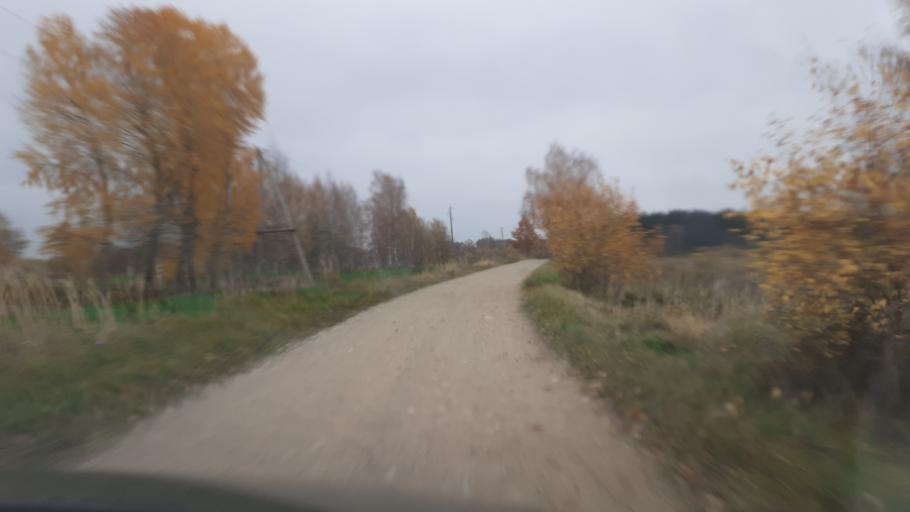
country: LV
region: Saldus Rajons
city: Saldus
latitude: 56.8630
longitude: 22.3259
